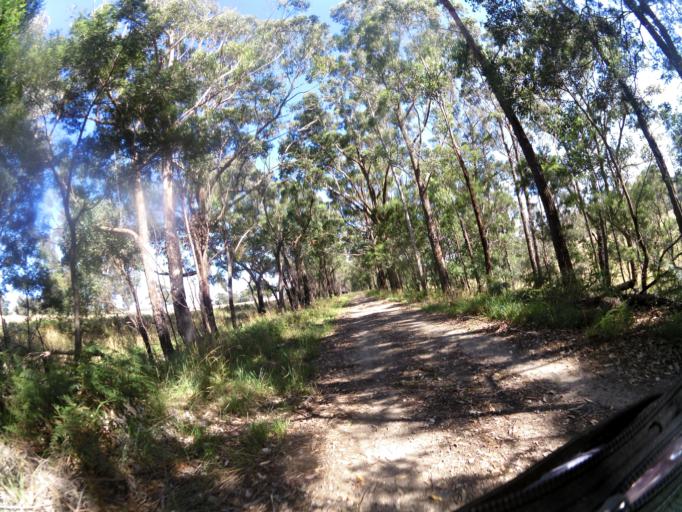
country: AU
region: Victoria
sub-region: East Gippsland
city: Lakes Entrance
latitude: -37.7447
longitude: 148.1743
